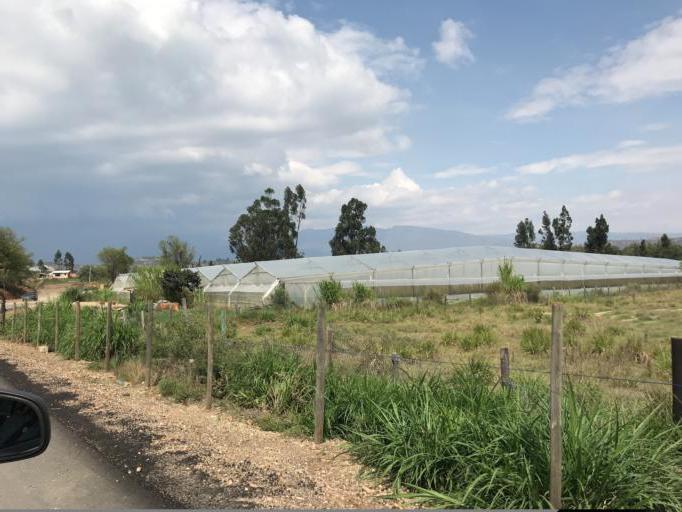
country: CO
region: Boyaca
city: Sutamarchan
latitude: 5.6294
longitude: -73.6108
